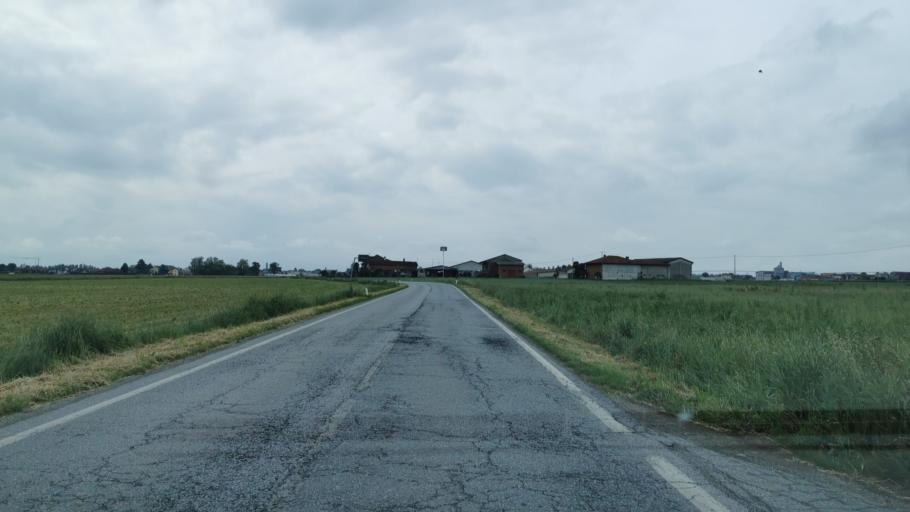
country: IT
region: Piedmont
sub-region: Provincia di Cuneo
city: Villafalletto
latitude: 44.5604
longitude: 7.5333
